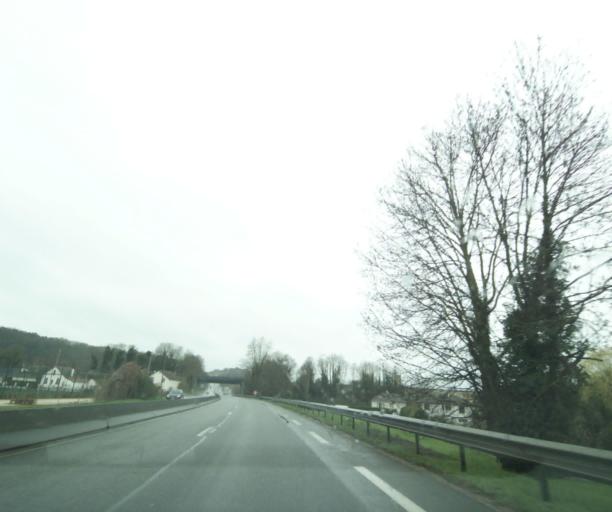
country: FR
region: Ile-de-France
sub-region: Departement de l'Essonne
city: Etampes
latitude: 48.4264
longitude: 2.1477
